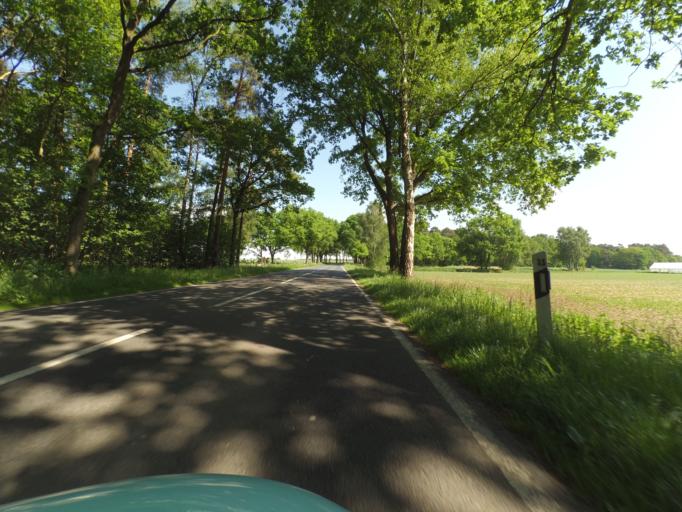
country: DE
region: Lower Saxony
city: Isernhagen Farster Bauerschaft
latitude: 52.4713
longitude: 9.8937
